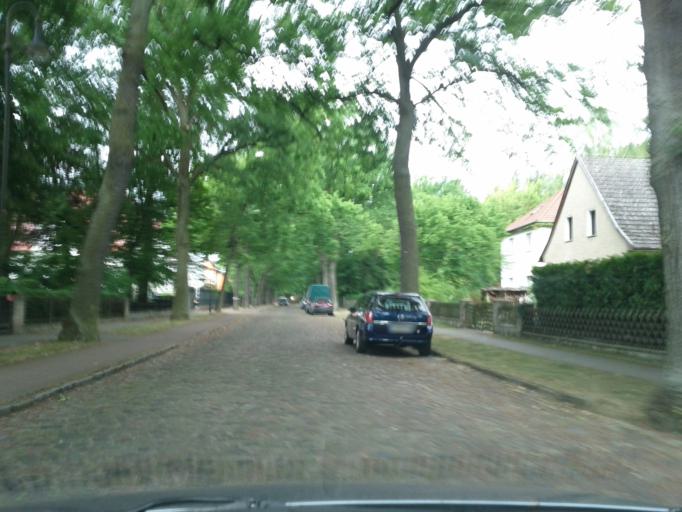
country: DE
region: Brandenburg
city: Schoneiche
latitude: 52.4651
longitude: 13.6934
